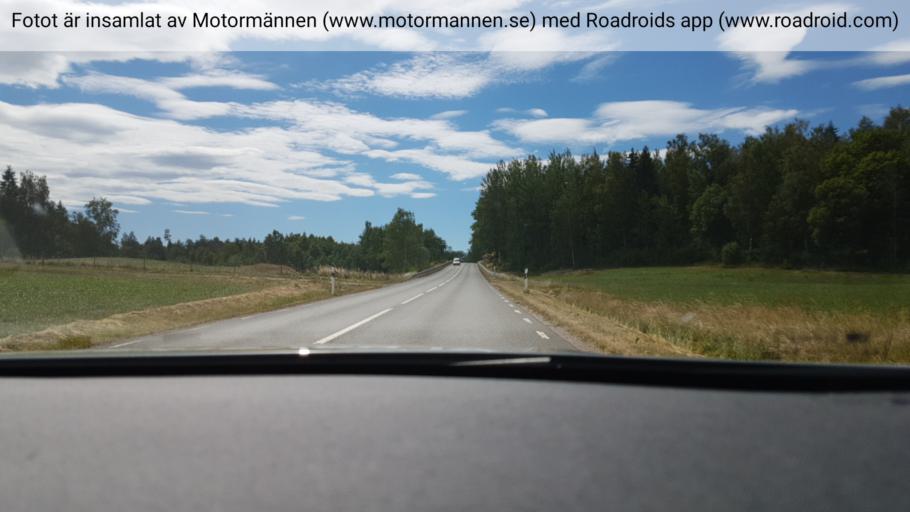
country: SE
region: Joenkoeping
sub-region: Aneby Kommun
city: Aneby
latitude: 57.9782
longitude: 14.8162
